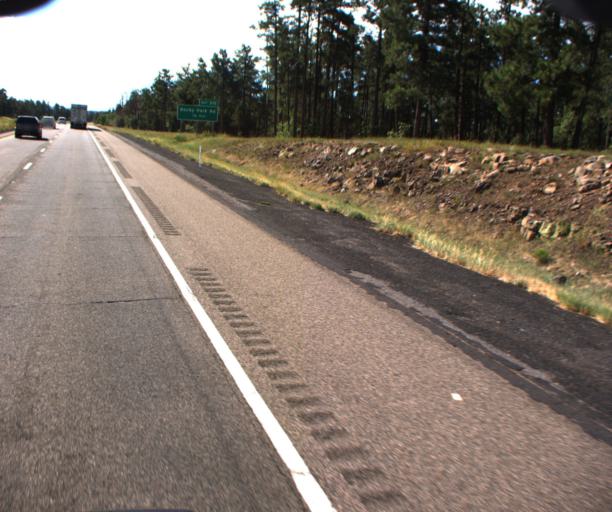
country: US
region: Arizona
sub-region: Coconino County
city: Sedona
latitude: 34.8614
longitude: -111.6166
